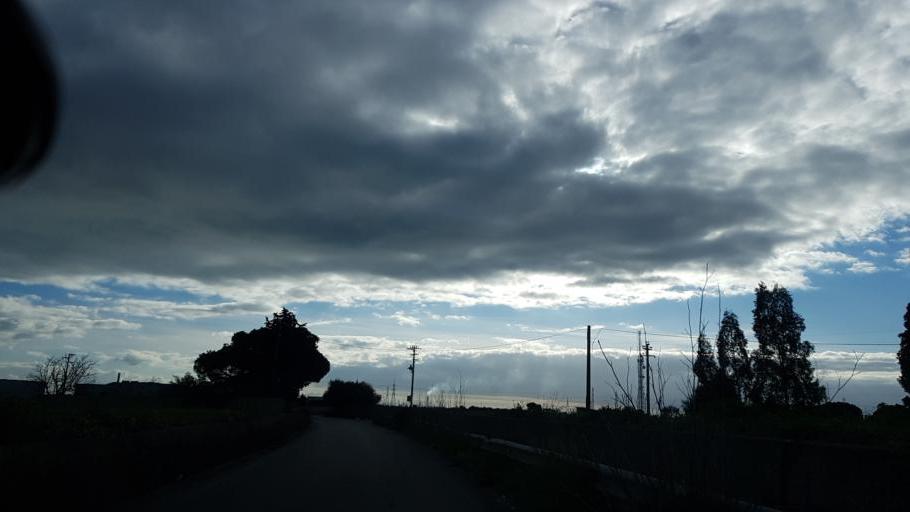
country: IT
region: Apulia
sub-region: Provincia di Brindisi
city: La Rosa
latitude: 40.6147
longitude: 17.9560
